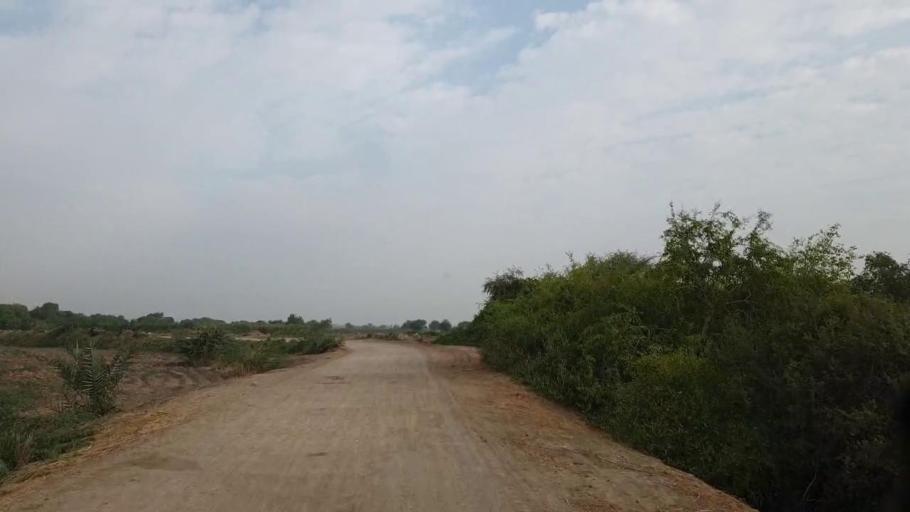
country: PK
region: Sindh
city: Tando Muhammad Khan
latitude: 25.0936
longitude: 68.4179
